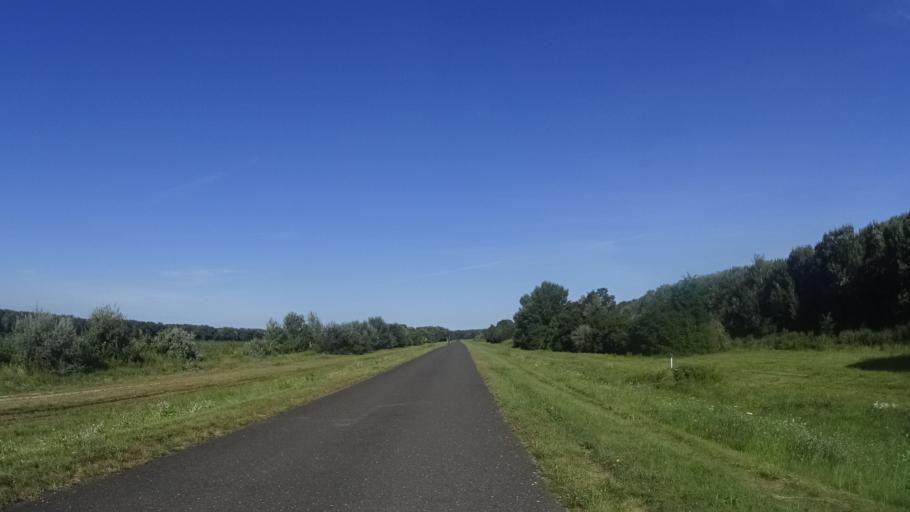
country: HU
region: Gyor-Moson-Sopron
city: Rajka
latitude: 48.0617
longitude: 17.1922
